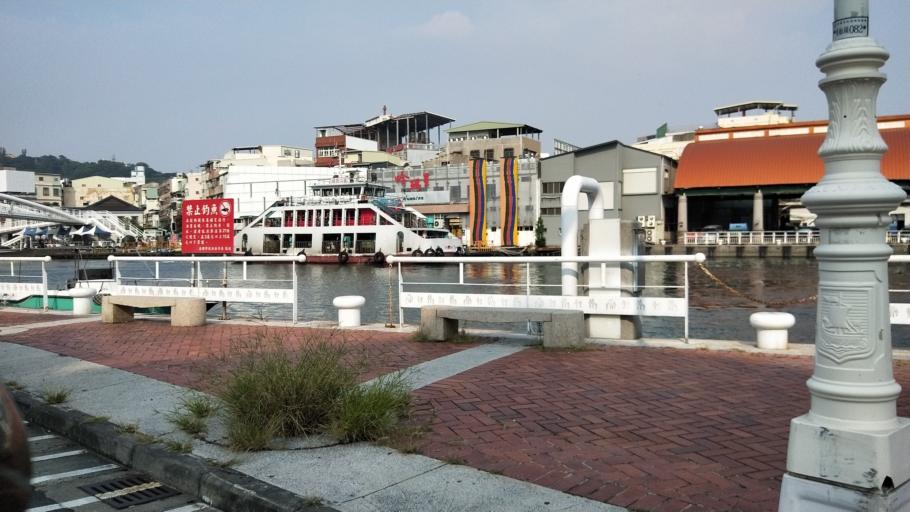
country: TW
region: Kaohsiung
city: Kaohsiung
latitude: 22.6193
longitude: 120.2693
